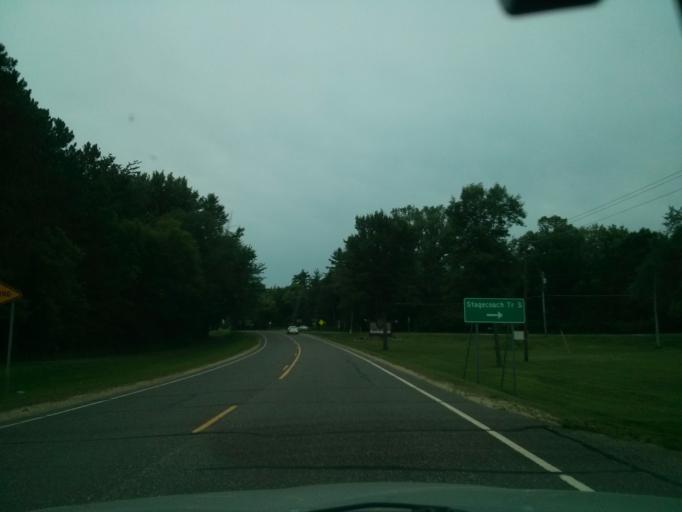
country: US
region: Minnesota
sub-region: Washington County
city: Afton
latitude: 44.9067
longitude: -92.7826
